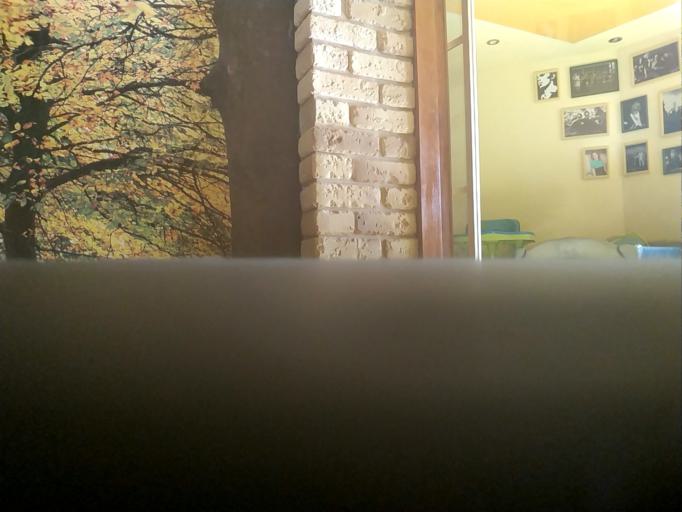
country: RU
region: Smolensk
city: Temkino
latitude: 55.0441
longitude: 34.9209
